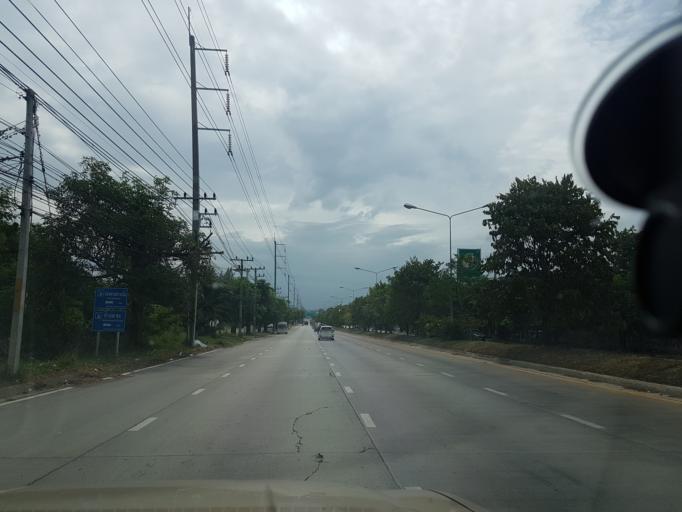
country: TH
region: Sara Buri
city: Phra Phutthabat
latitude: 14.7191
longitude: 100.8101
